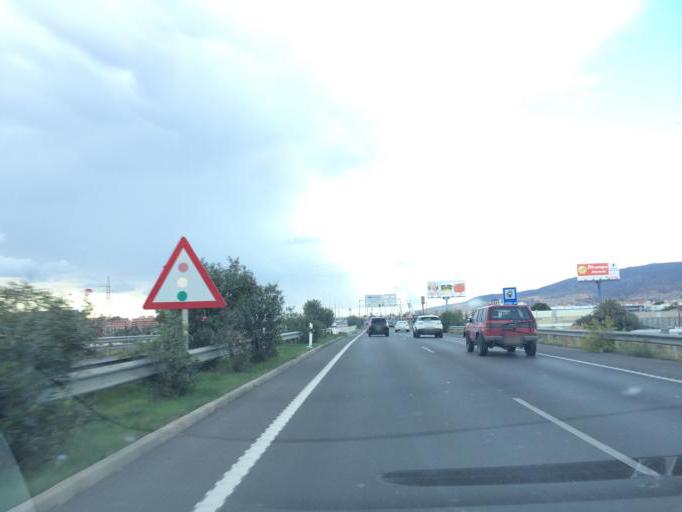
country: ES
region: Andalusia
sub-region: Provincia de Almeria
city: Almeria
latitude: 36.8426
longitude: -2.4269
